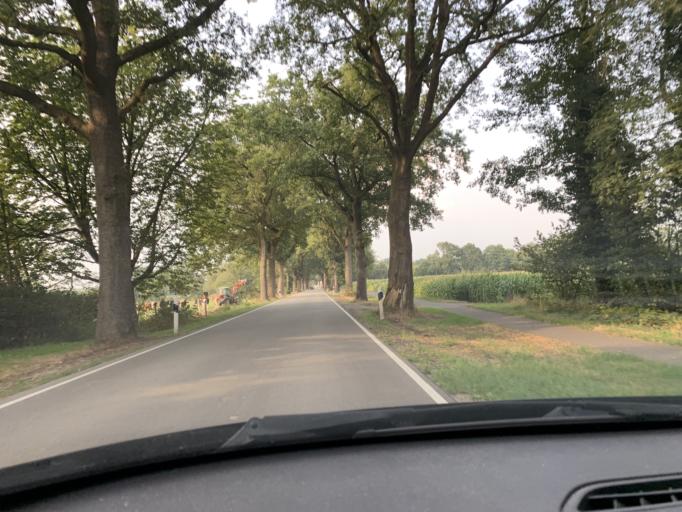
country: DE
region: Lower Saxony
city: Apen
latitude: 53.2079
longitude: 7.7948
